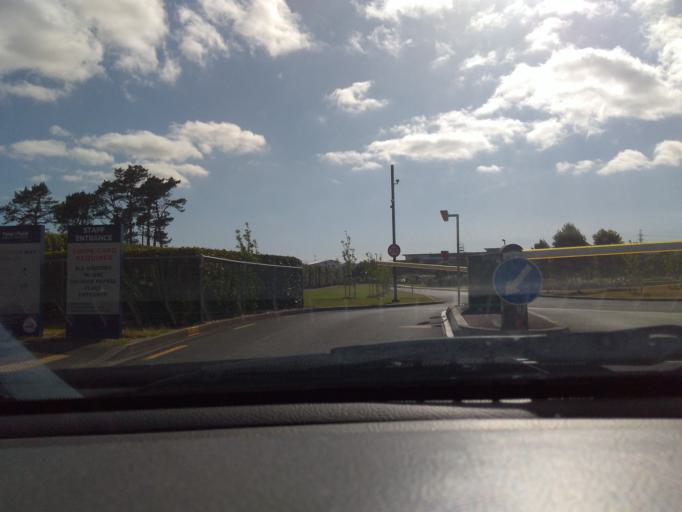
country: NZ
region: Auckland
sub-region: Auckland
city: Tamaki
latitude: -36.9332
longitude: 174.8776
